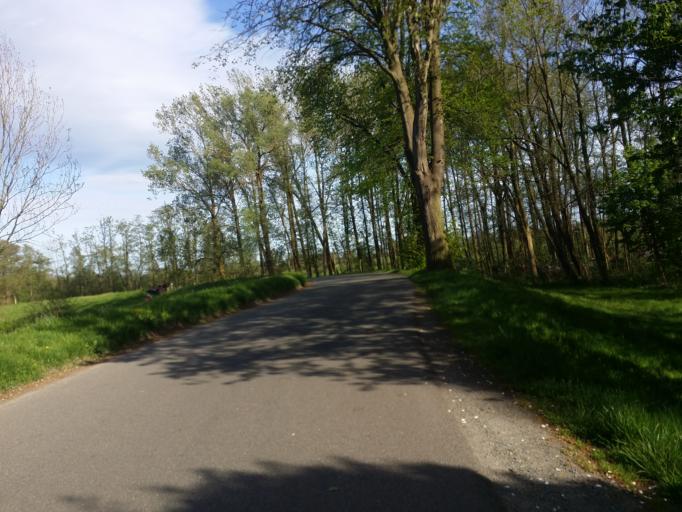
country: DE
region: Lower Saxony
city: Ritterhude
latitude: 53.1635
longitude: 8.7414
